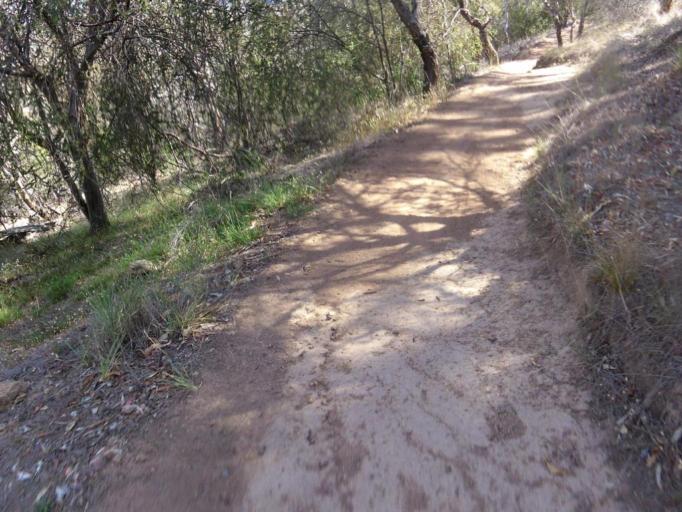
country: AU
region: Australian Capital Territory
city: Belconnen
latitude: -35.1576
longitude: 149.0789
